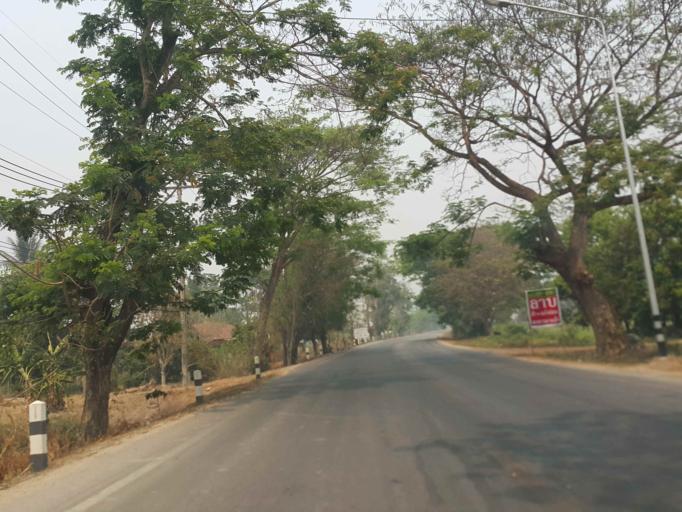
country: TH
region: Chiang Mai
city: Mae Taeng
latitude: 19.0507
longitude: 98.9620
